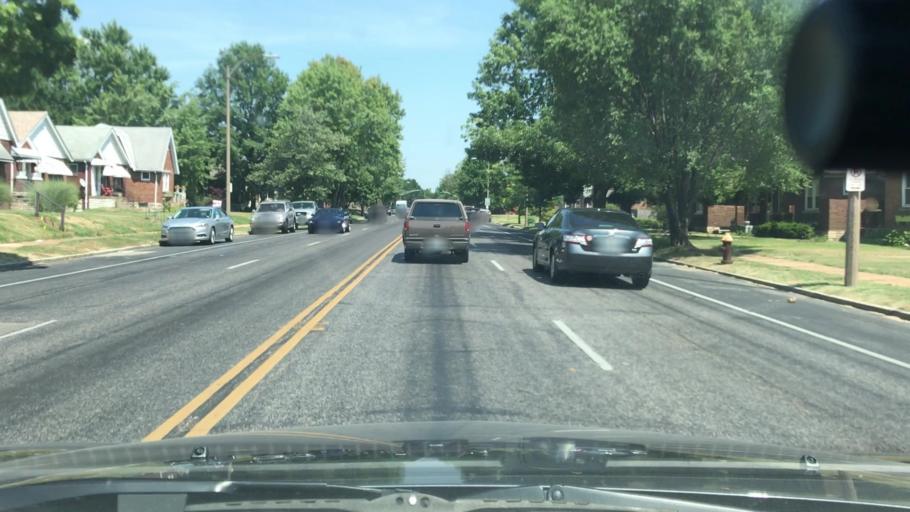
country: US
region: Missouri
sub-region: Saint Louis County
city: Maplewood
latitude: 38.5921
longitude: -90.2821
